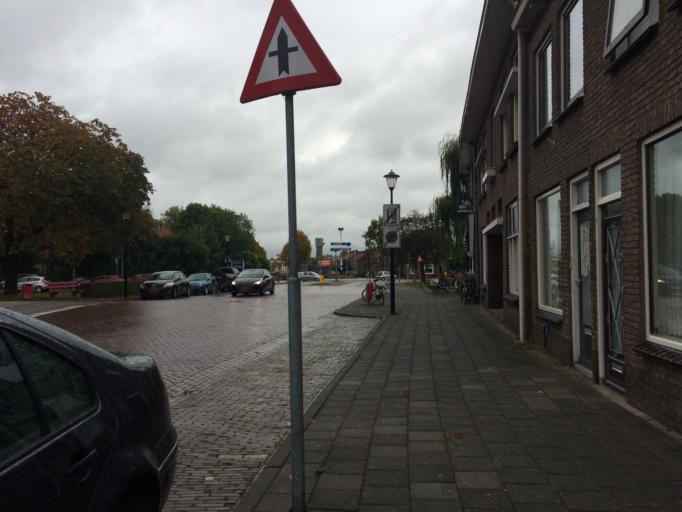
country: NL
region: Gelderland
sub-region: Gemeente Culemborg
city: Culemborg
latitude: 51.9531
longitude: 5.2288
